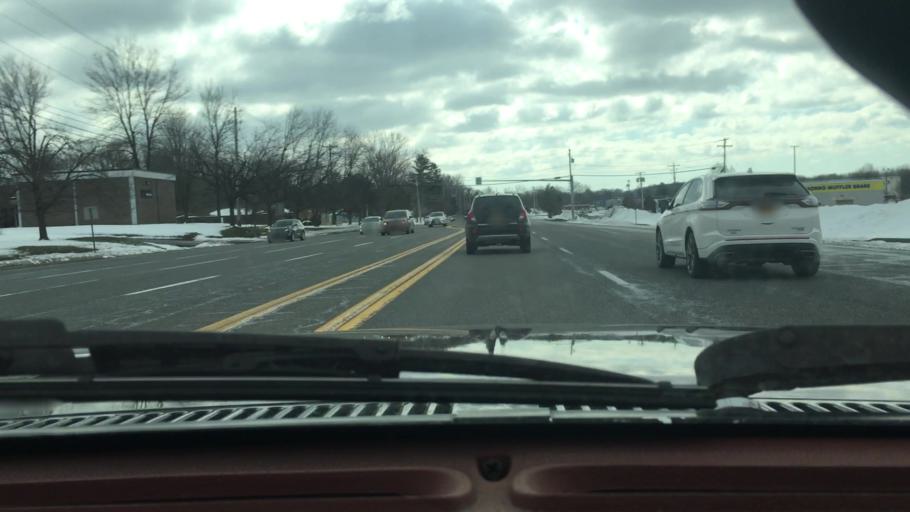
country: US
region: New York
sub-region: Onondaga County
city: Liverpool
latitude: 43.1627
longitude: -76.2344
